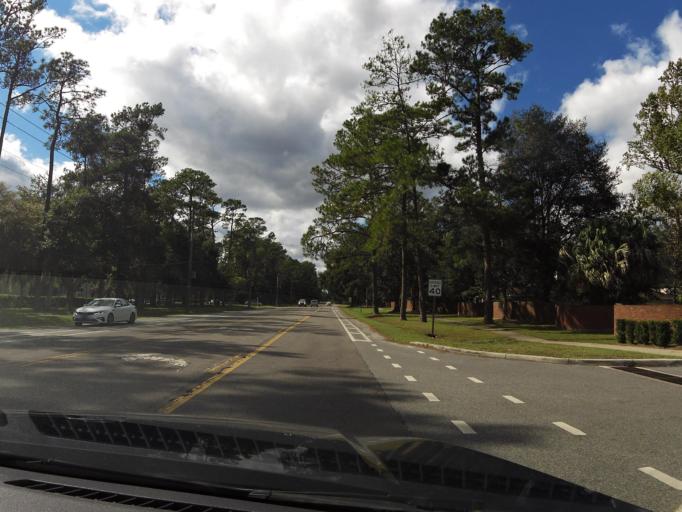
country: US
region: Florida
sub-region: Alachua County
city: Alachua
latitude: 29.7033
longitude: -82.3898
